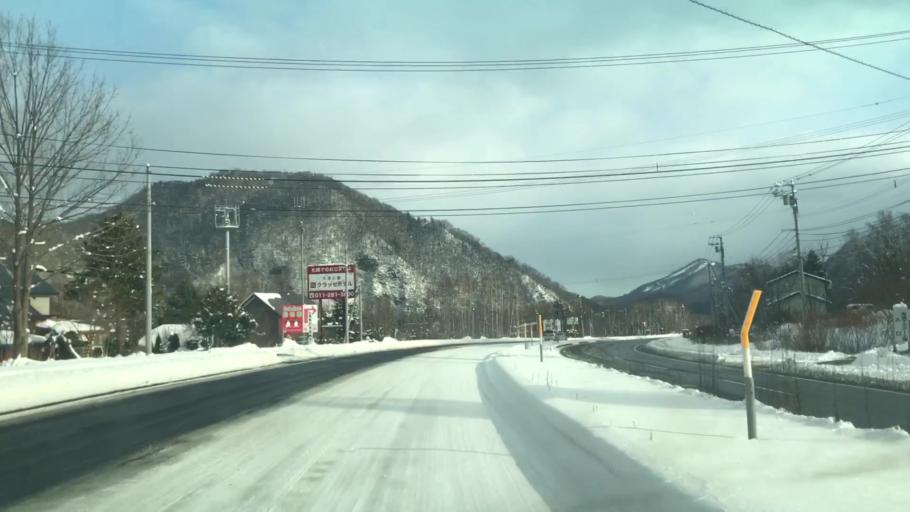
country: JP
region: Hokkaido
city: Sapporo
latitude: 42.9696
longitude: 141.2098
